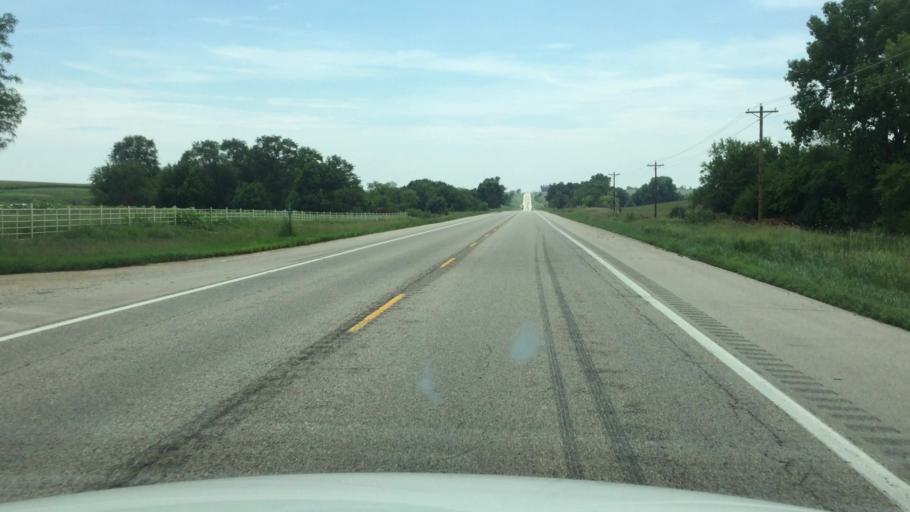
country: US
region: Kansas
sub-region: Brown County
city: Horton
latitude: 39.6945
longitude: -95.7303
